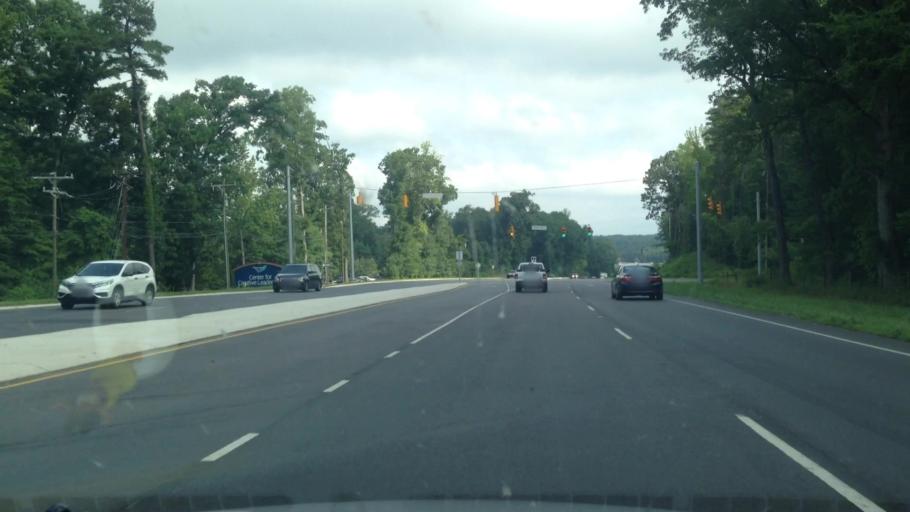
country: US
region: North Carolina
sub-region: Guilford County
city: Summerfield
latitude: 36.1629
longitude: -79.8772
